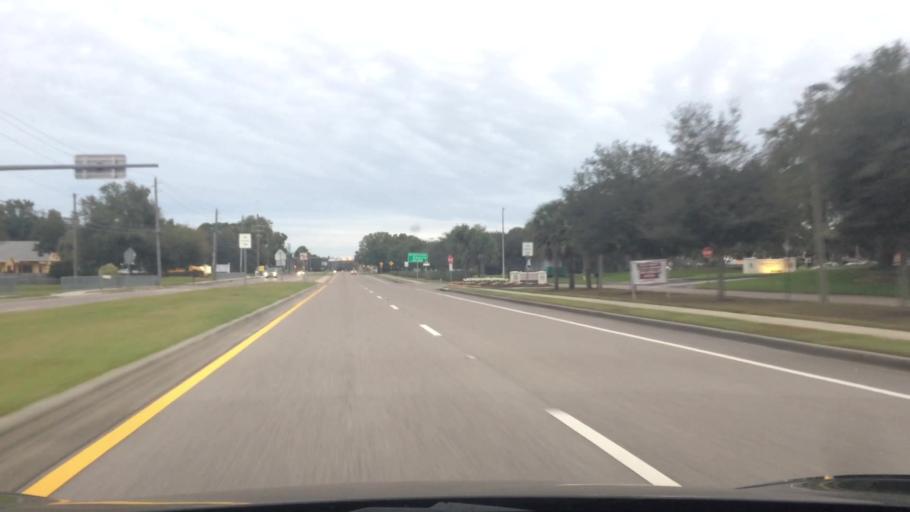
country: US
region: Florida
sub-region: Hillsborough County
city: Cheval
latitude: 28.1555
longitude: -82.5292
